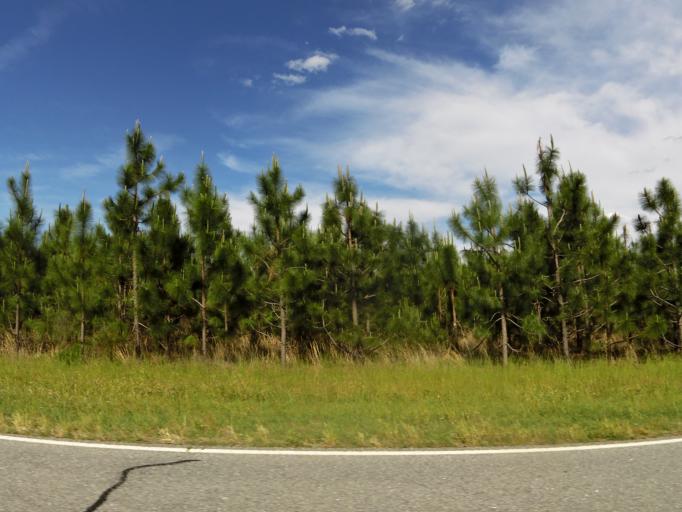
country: US
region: South Carolina
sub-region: Allendale County
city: Allendale
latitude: 33.1420
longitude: -81.1895
